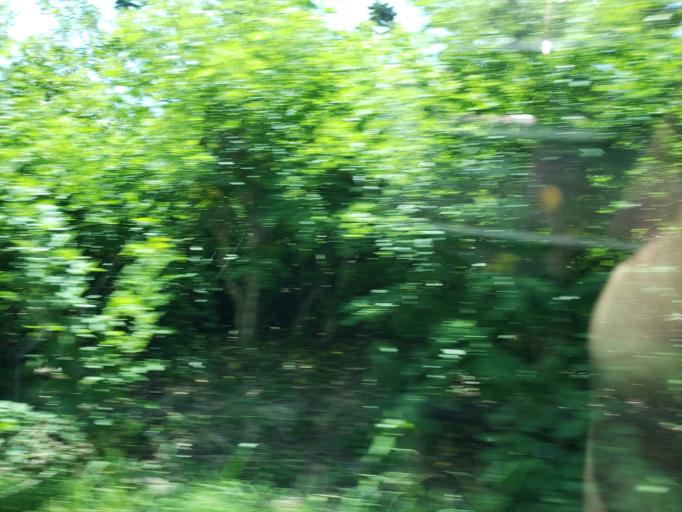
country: ID
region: Bali
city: Kangin
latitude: -8.8401
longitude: 115.1400
